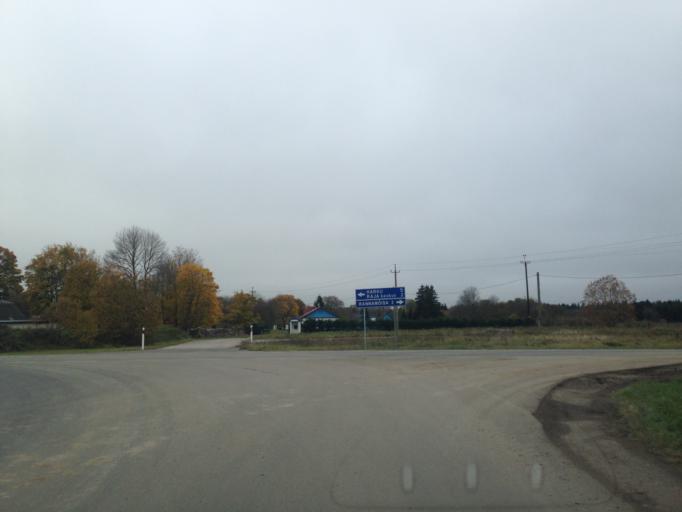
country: EE
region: Harju
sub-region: Harku vald
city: Tabasalu
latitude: 59.4217
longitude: 24.5383
